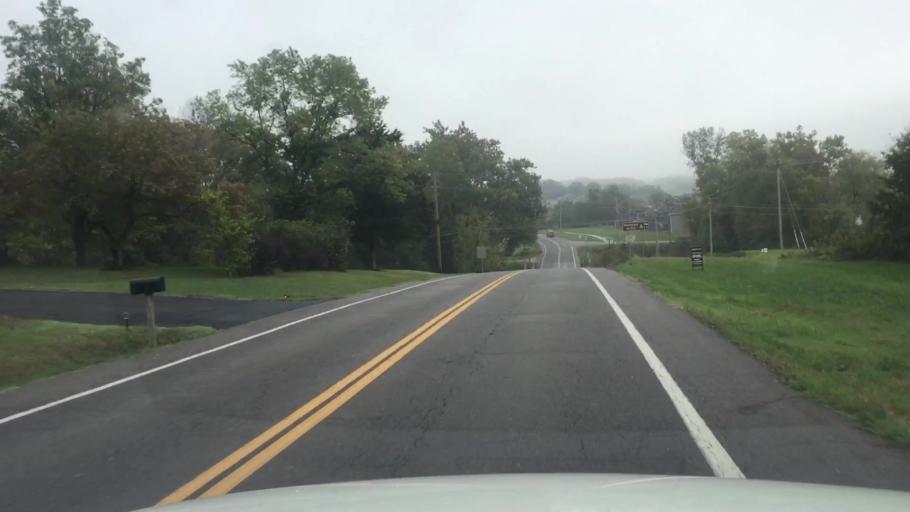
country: US
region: Missouri
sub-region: Boone County
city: Columbia
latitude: 38.8708
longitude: -92.3849
